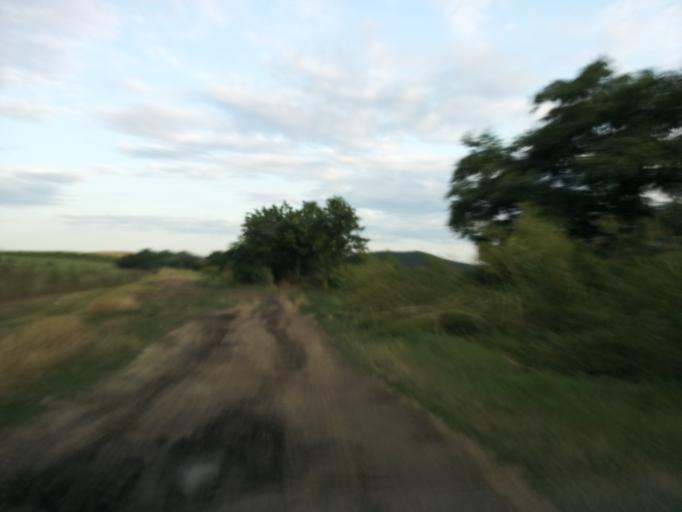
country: HU
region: Fejer
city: Lajoskomarom
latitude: 46.7998
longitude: 18.2492
